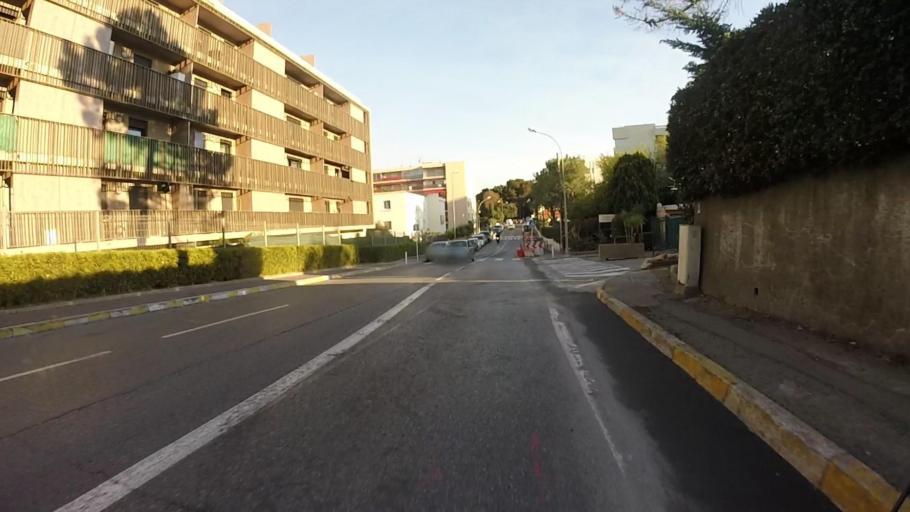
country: FR
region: Provence-Alpes-Cote d'Azur
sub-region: Departement des Alpes-Maritimes
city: Biot
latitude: 43.5987
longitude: 7.0920
